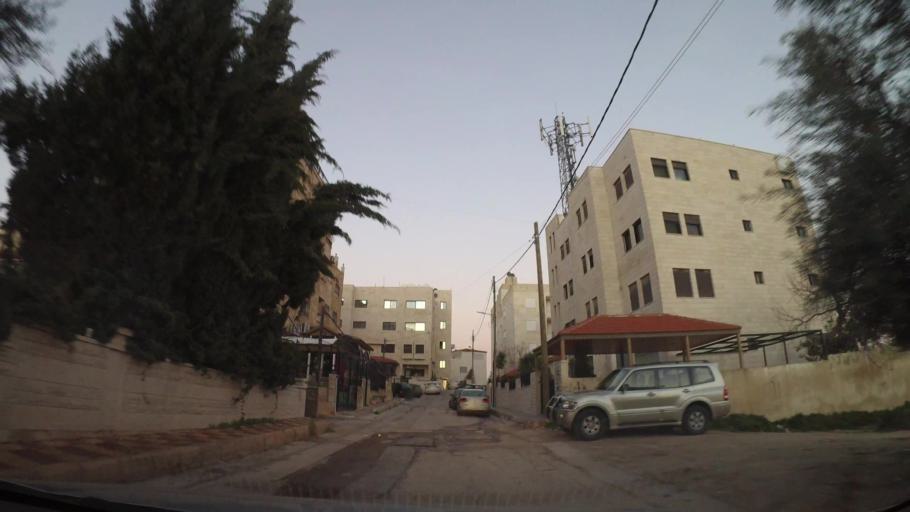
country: JO
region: Amman
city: Al Jubayhah
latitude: 31.9995
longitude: 35.8539
